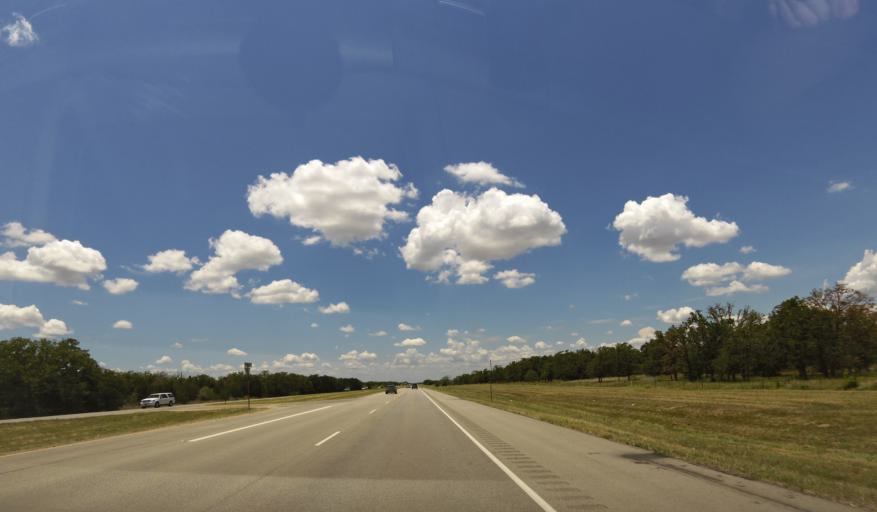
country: US
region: Texas
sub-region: Lee County
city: Giddings
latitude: 30.1430
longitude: -96.7713
